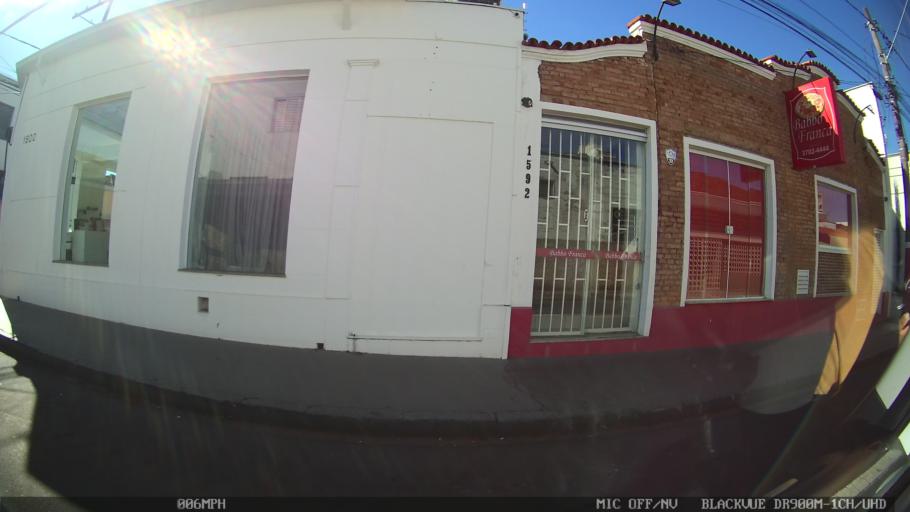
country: BR
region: Sao Paulo
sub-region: Franca
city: Franca
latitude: -20.5404
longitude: -47.3996
